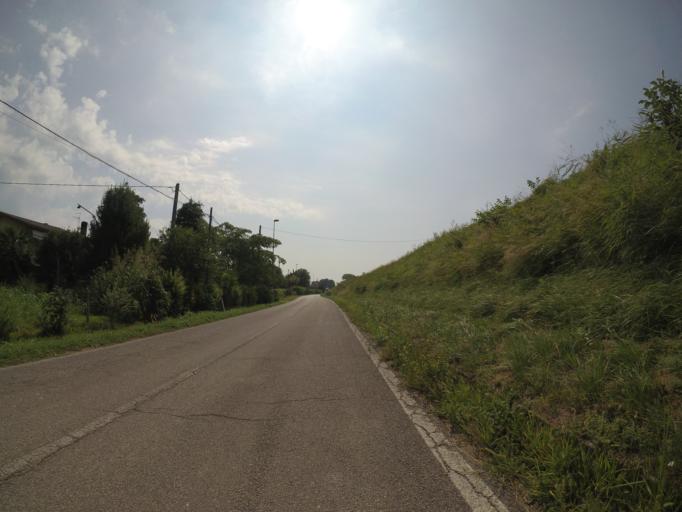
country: IT
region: Friuli Venezia Giulia
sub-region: Provincia di Udine
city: Pertegada
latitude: 45.7062
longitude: 13.0440
